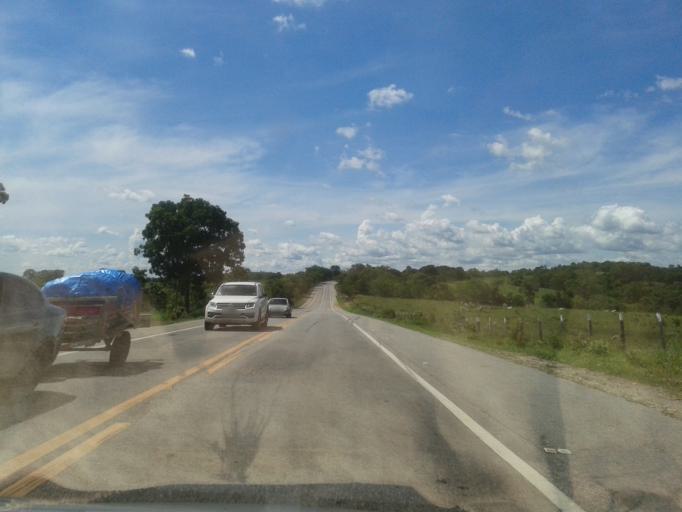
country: BR
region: Goias
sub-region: Goias
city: Goias
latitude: -15.7433
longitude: -50.1788
